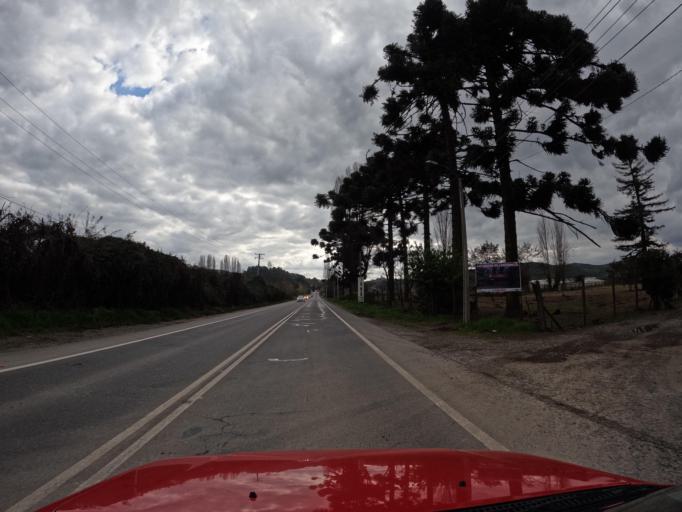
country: CL
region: Maule
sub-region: Provincia de Linares
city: San Javier
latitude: -35.6231
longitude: -71.7598
